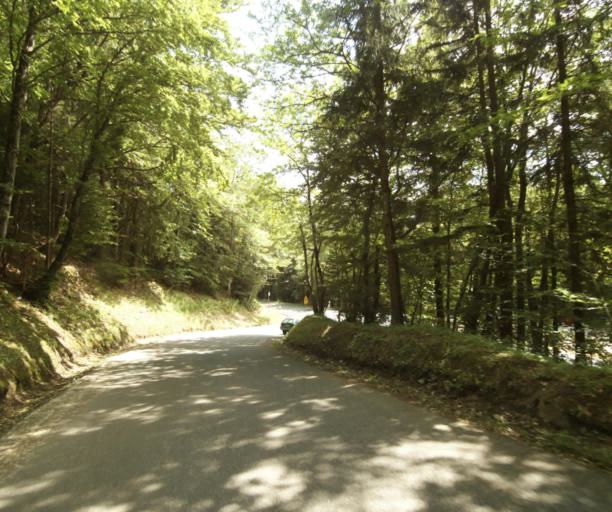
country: FR
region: Rhone-Alpes
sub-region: Departement de la Haute-Savoie
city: Perrignier
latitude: 46.2998
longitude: 6.4637
